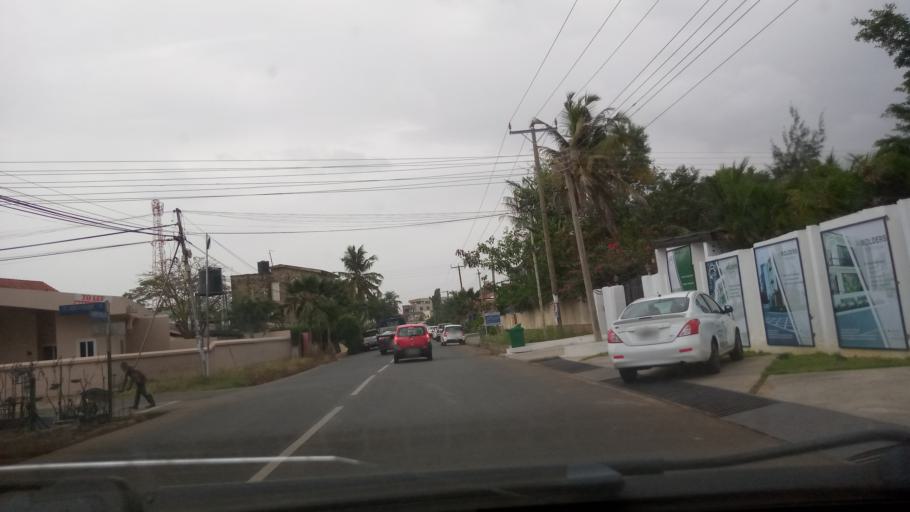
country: GH
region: Greater Accra
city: Dome
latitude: 5.6158
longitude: -0.1999
